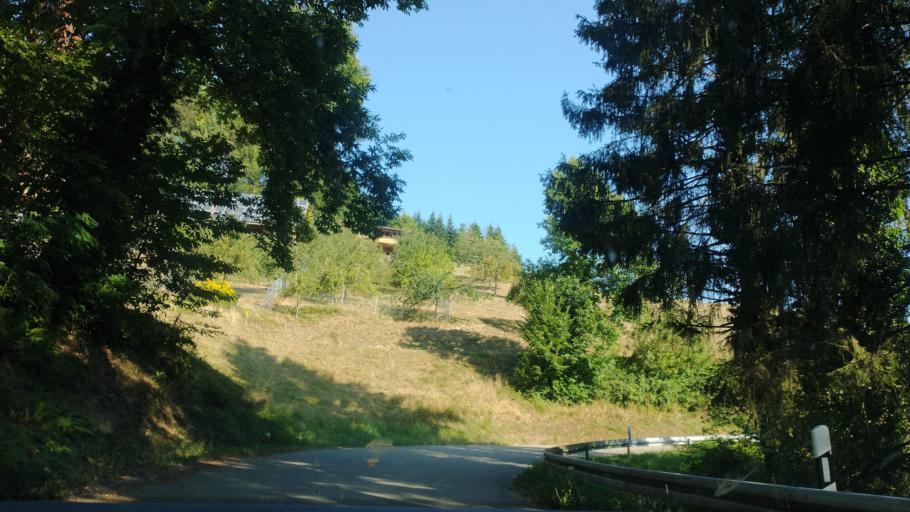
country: DE
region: Baden-Wuerttemberg
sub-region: Freiburg Region
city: Biberach
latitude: 48.3284
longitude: 8.0059
